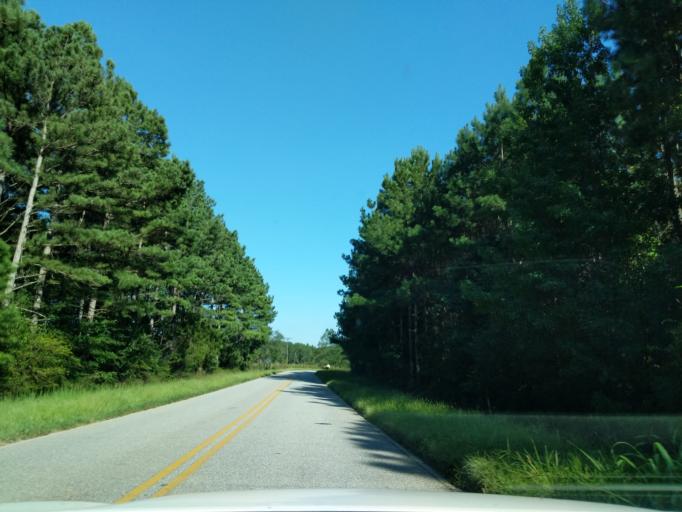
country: US
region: Georgia
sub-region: Oglethorpe County
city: Lexington
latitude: 33.9193
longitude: -83.0224
